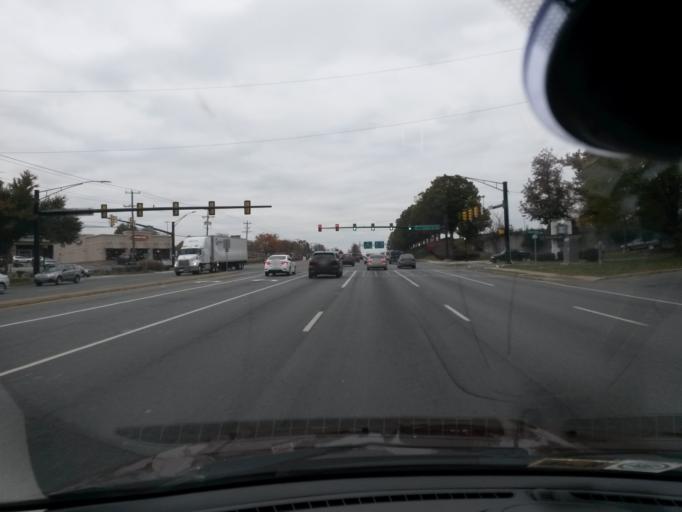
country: US
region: Virginia
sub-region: City of Charlottesville
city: Charlottesville
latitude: 38.0762
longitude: -78.4788
